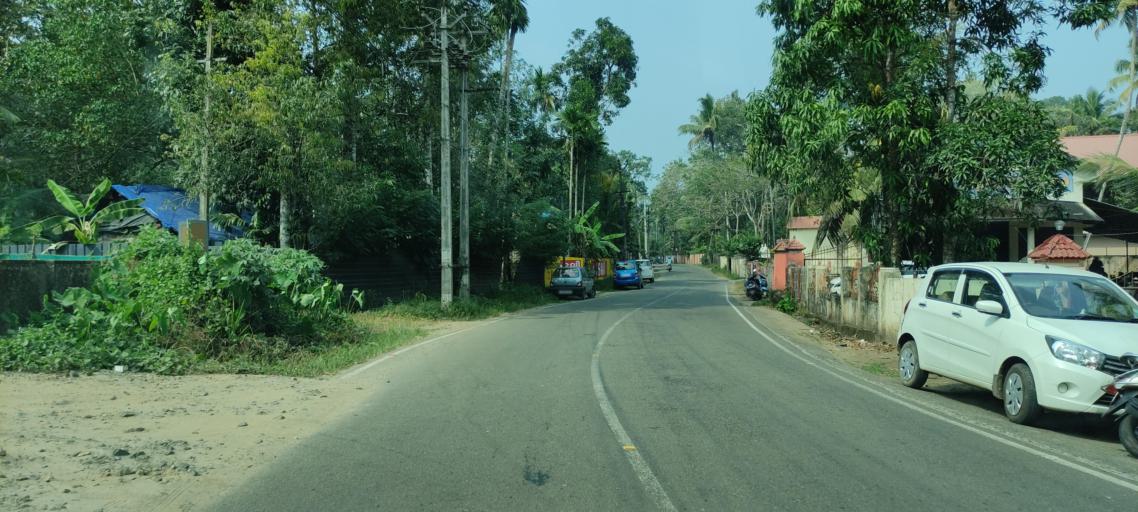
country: IN
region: Kerala
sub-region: Kottayam
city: Vaikam
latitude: 9.7282
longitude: 76.4150
